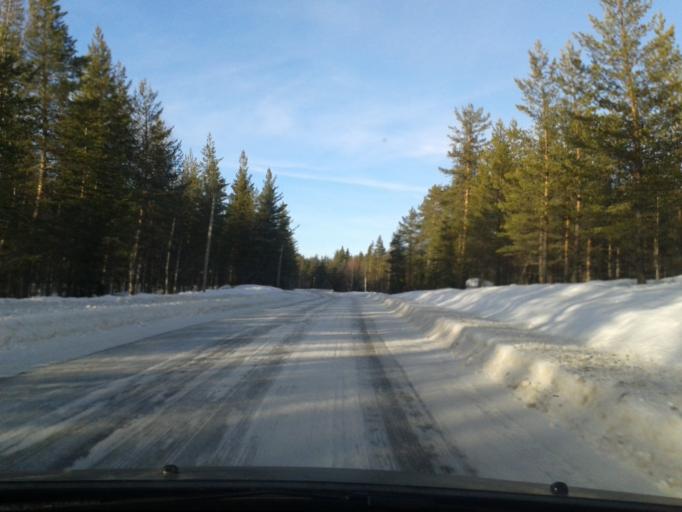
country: SE
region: Vaesternorrland
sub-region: OErnskoeldsviks Kommun
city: Bredbyn
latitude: 63.7309
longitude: 17.7460
